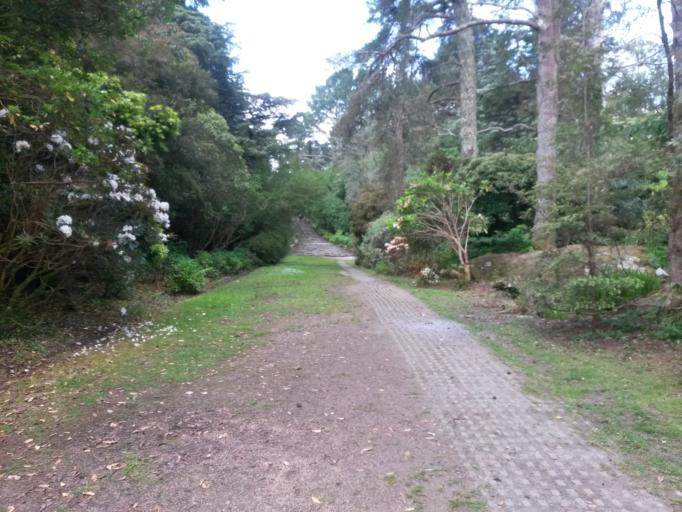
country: IE
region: Munster
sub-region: County Cork
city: Bantry
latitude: 51.7354
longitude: -9.5451
